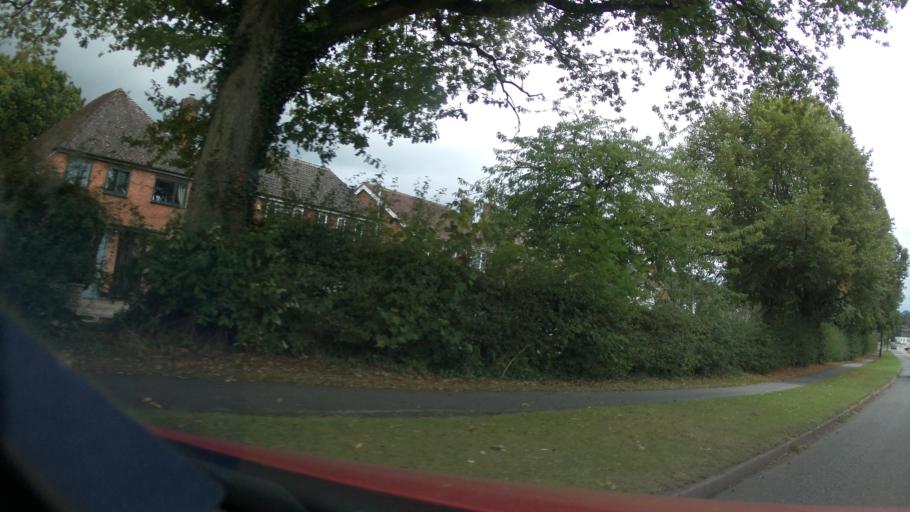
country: GB
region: England
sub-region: Solihull
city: Cheswick Green
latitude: 52.3569
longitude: -1.7791
